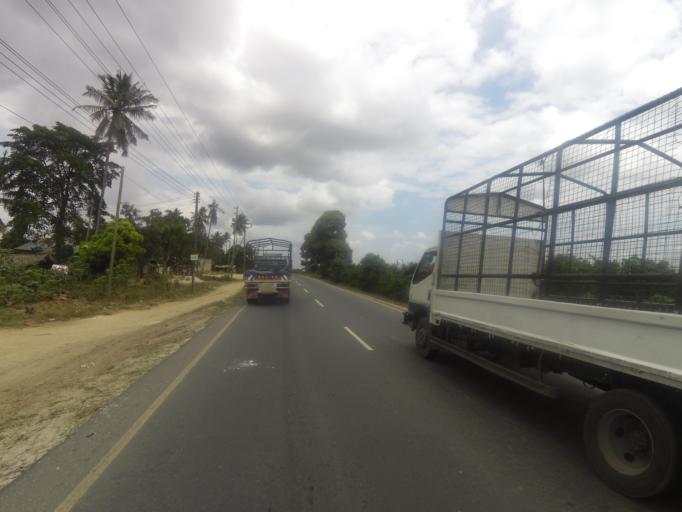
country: TZ
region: Pwani
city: Vikindu
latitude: -6.9651
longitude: 39.2852
